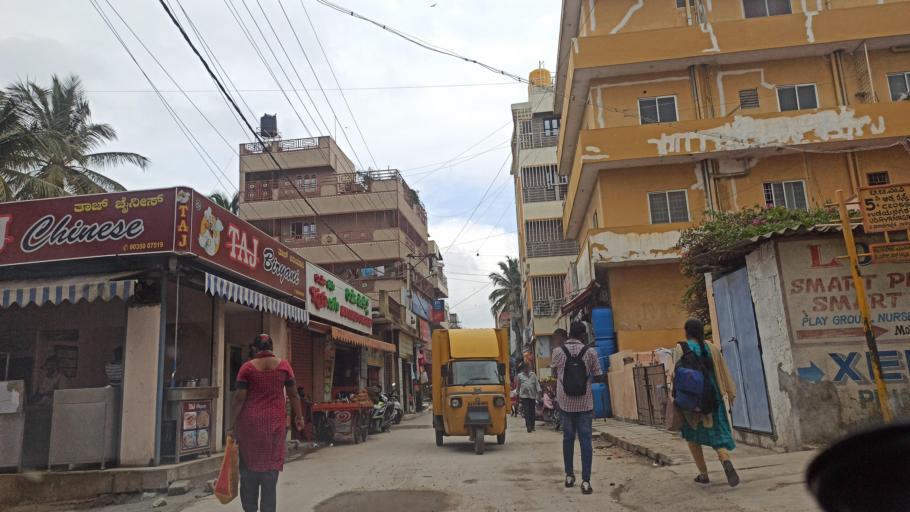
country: IN
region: Karnataka
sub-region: Bangalore Urban
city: Bangalore
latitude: 12.9949
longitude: 77.6726
